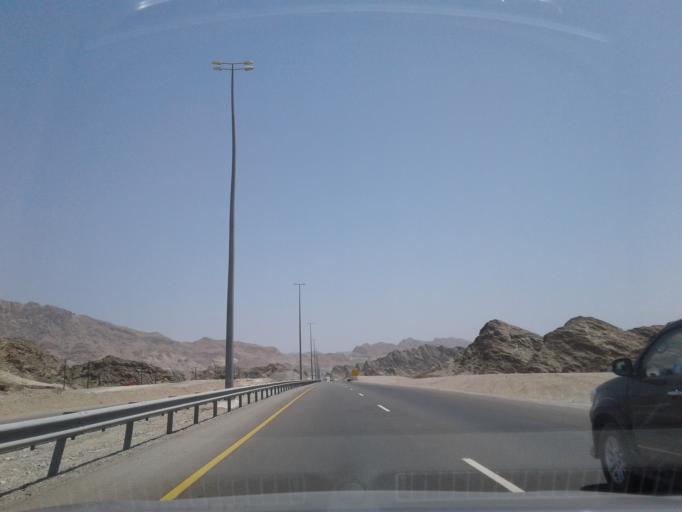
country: OM
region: Muhafazat Masqat
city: Bawshar
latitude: 23.4636
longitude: 58.4954
